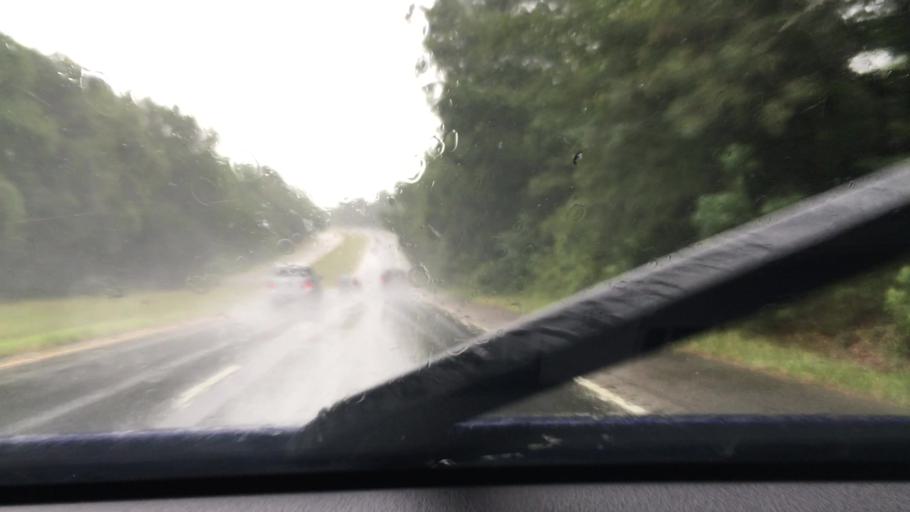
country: US
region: South Carolina
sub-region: Sumter County
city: Stateburg
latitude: 33.9452
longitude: -80.5209
